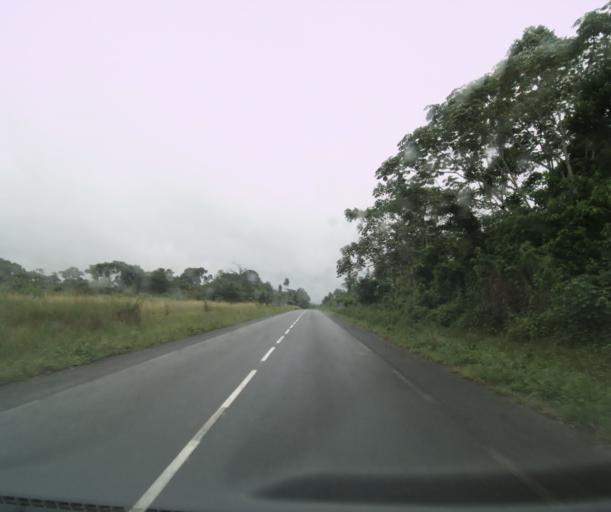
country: CM
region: Littoral
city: Dizangue
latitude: 3.3575
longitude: 10.1016
